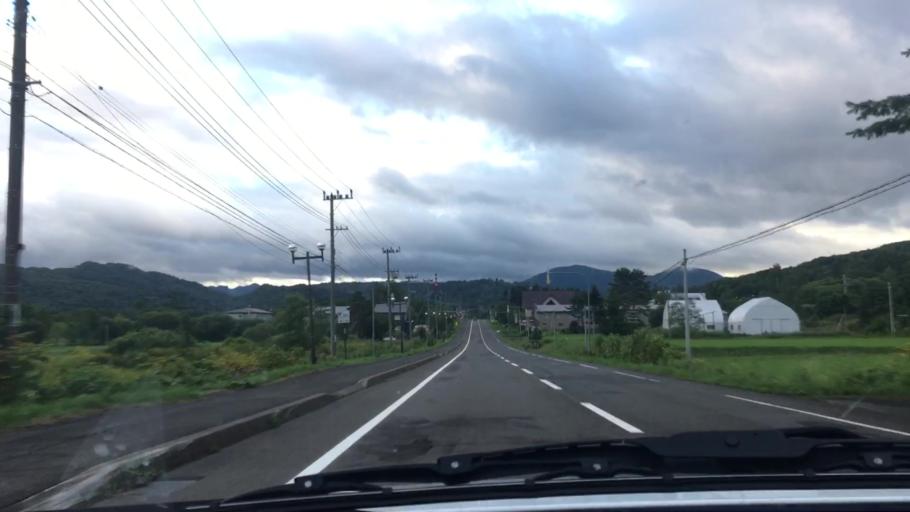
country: JP
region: Hokkaido
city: Shimo-furano
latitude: 42.9959
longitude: 142.4032
